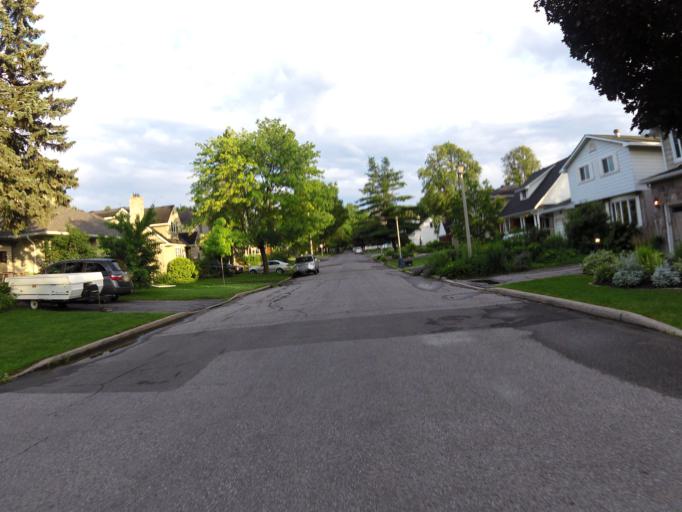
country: CA
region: Ontario
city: Ottawa
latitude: 45.3817
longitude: -75.7671
